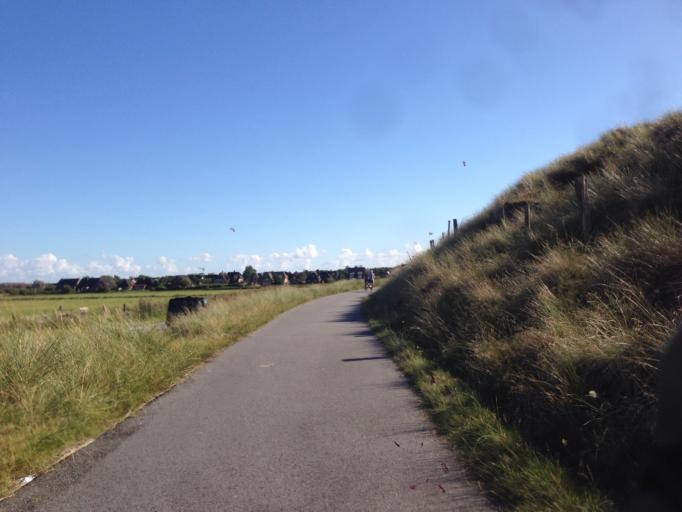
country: DE
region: Schleswig-Holstein
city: List
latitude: 55.0276
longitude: 8.4186
